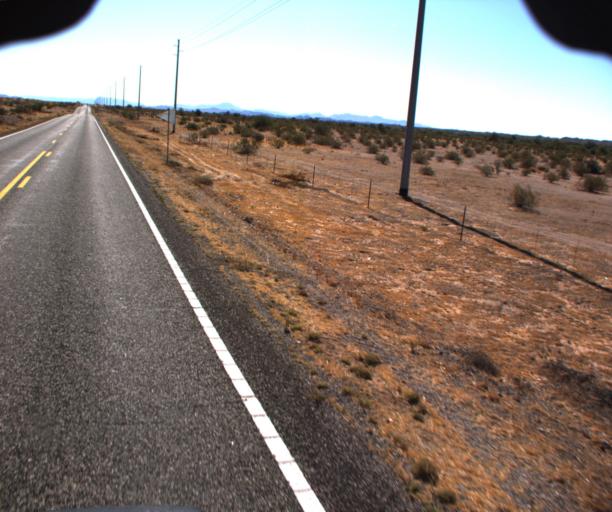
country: US
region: Arizona
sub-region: La Paz County
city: Cienega Springs
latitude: 33.9934
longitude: -114.1202
